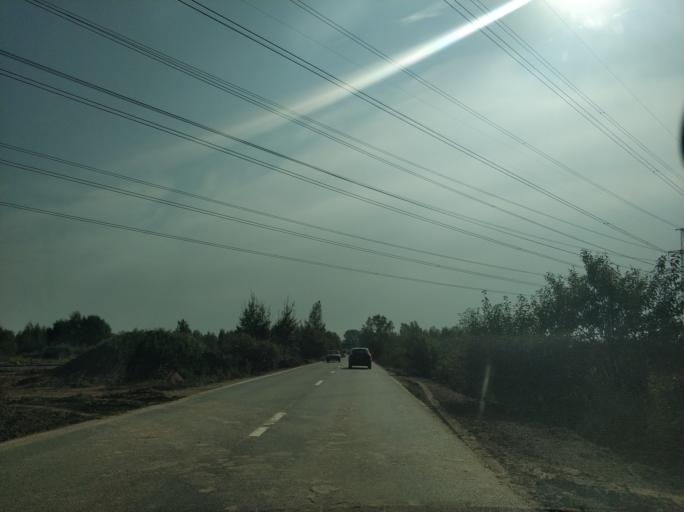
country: RU
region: St.-Petersburg
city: Krasnogvargeisky
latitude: 60.0093
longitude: 30.4841
